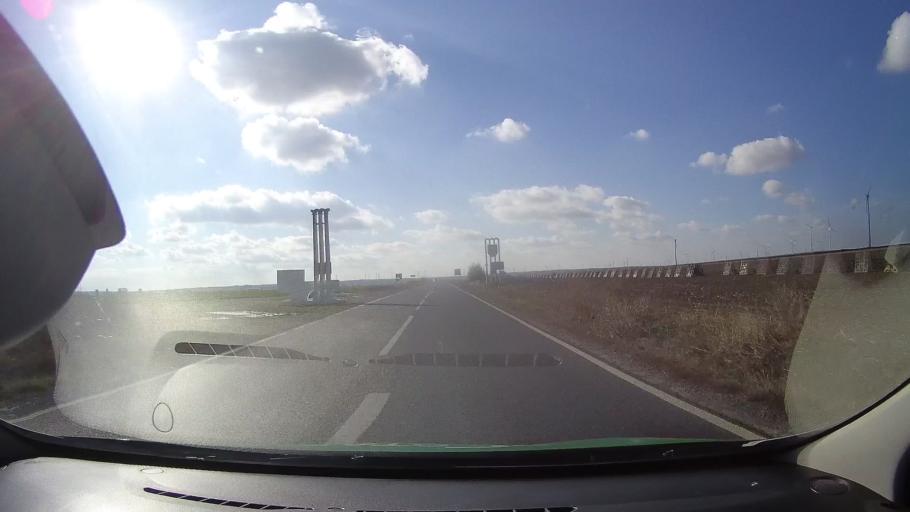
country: RO
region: Constanta
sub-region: Comuna Mihai Viteazu
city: Mihai Viteazu
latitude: 44.6659
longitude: 28.6813
